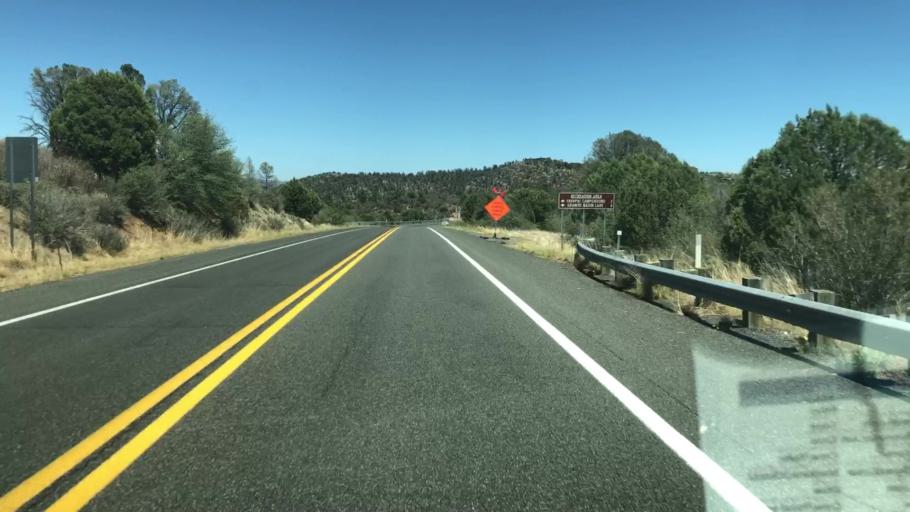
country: US
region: Arizona
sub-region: Yavapai County
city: Prescott
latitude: 34.5783
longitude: -112.5263
